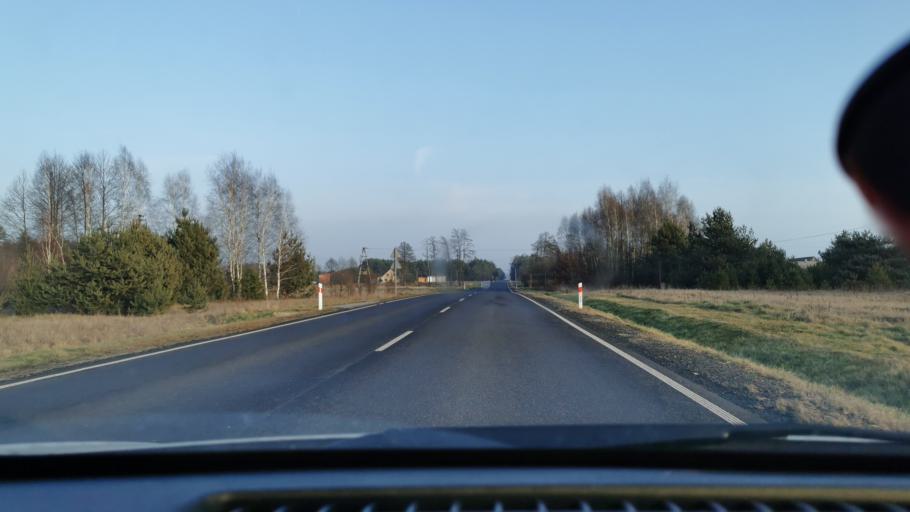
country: PL
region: Lodz Voivodeship
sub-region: Powiat pabianicki
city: Dlutow
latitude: 51.5122
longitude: 19.3402
